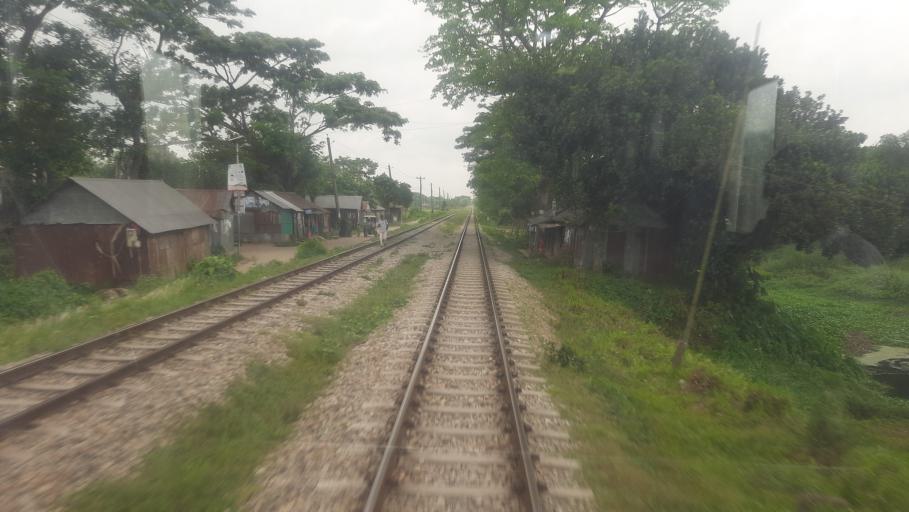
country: BD
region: Dhaka
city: Bhairab Bazar
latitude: 23.9860
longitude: 91.0701
